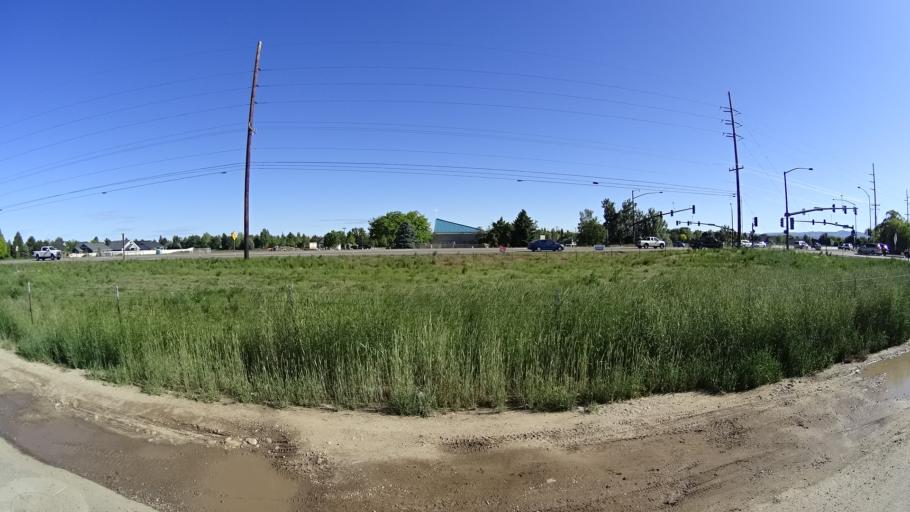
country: US
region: Idaho
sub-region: Ada County
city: Eagle
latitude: 43.6934
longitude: -116.4144
